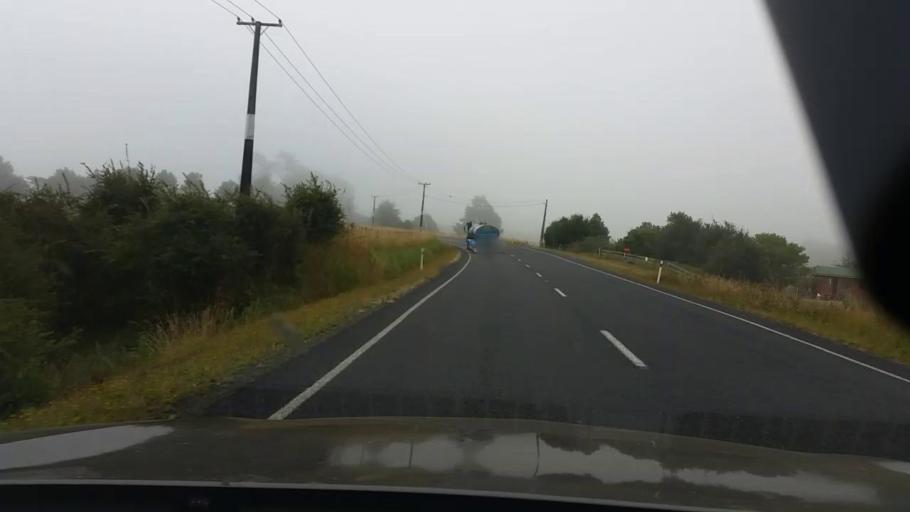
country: NZ
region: Waikato
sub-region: Hamilton City
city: Hamilton
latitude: -37.6442
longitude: 175.2954
